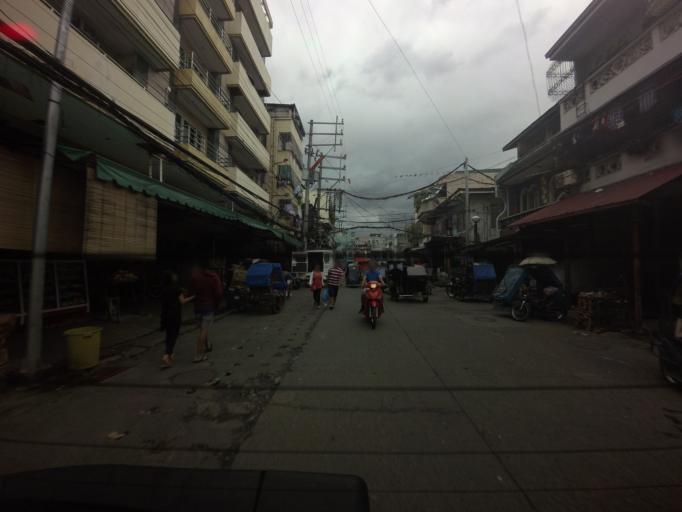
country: PH
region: Metro Manila
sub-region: City of Manila
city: Manila
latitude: 14.6043
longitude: 120.9661
